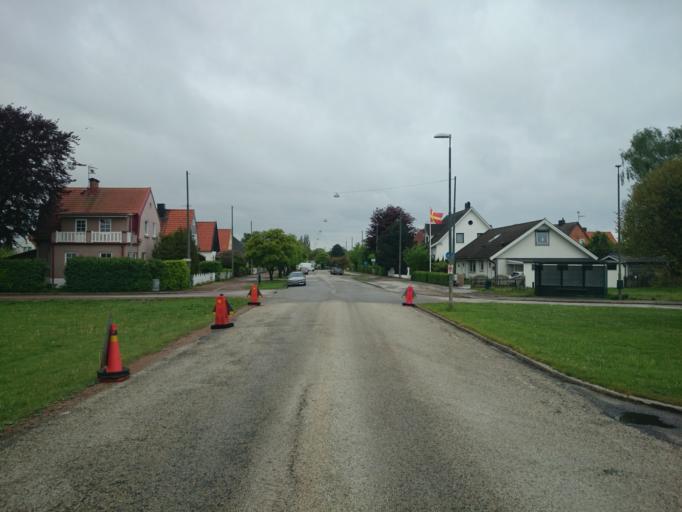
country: SE
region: Skane
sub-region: Burlovs Kommun
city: Arloev
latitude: 55.6106
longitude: 13.0779
